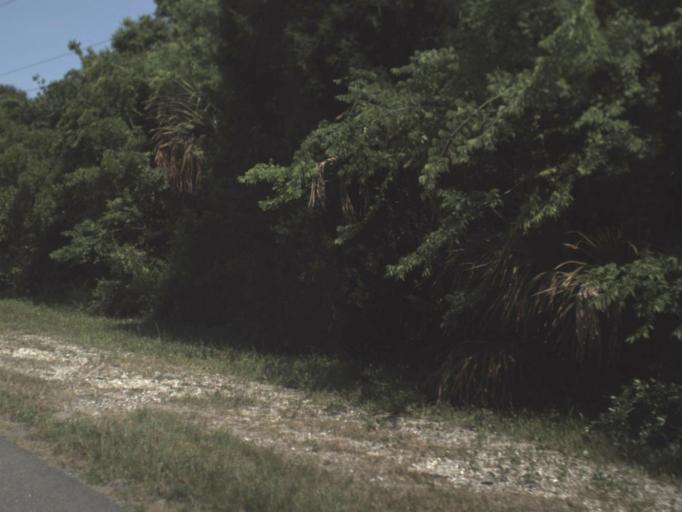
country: US
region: Florida
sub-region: Duval County
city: Atlantic Beach
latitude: 30.3983
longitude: -81.4948
